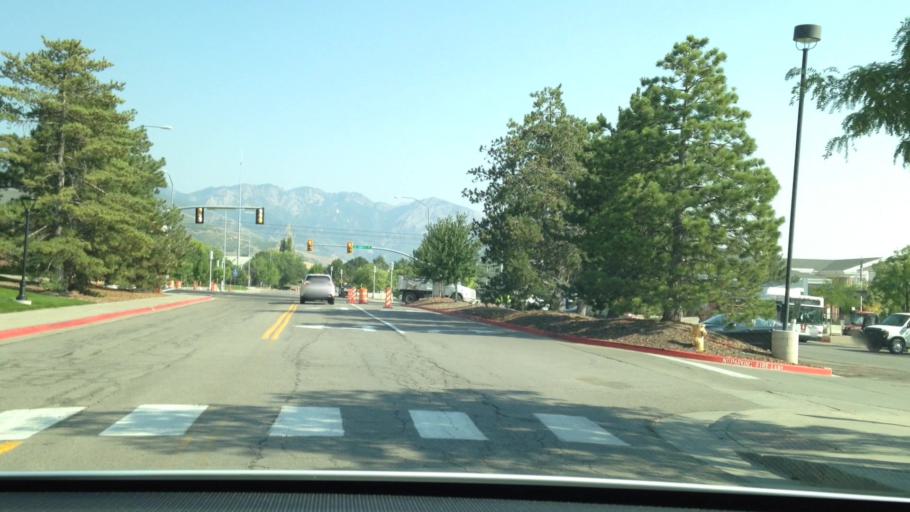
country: US
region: Utah
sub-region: Salt Lake County
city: Salt Lake City
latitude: 40.7613
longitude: -111.8395
